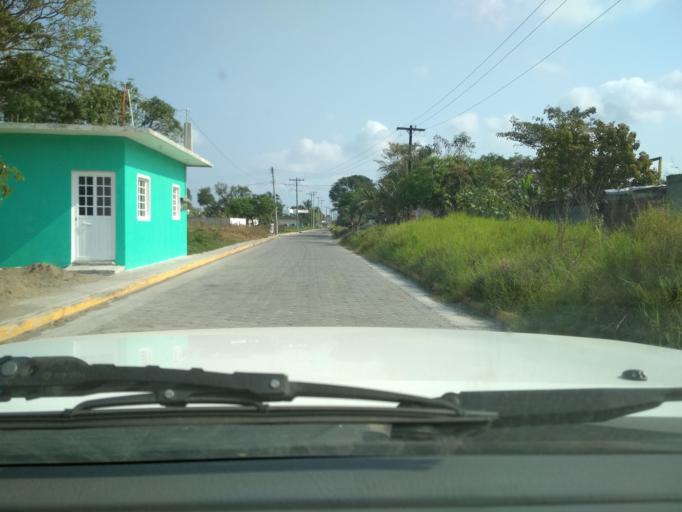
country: MX
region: Veracruz
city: El Tejar
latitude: 19.0804
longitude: -96.1609
